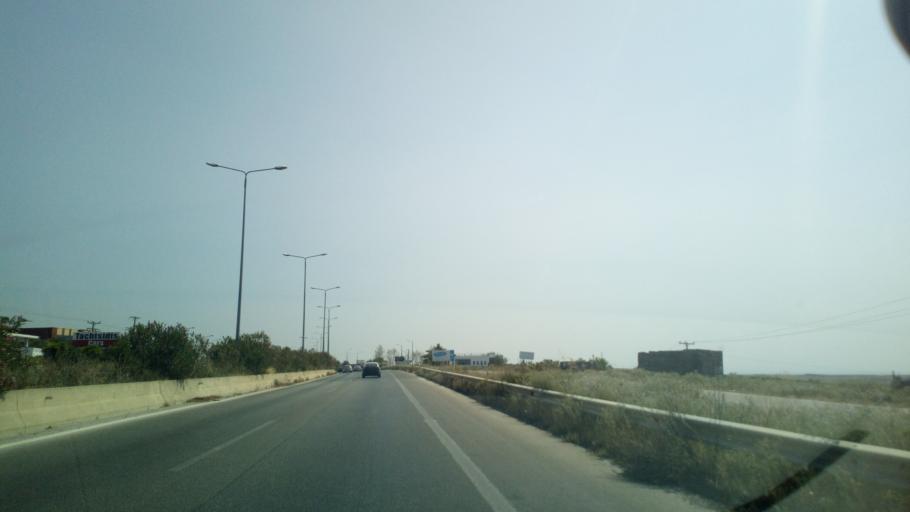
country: GR
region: Central Macedonia
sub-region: Nomos Thessalonikis
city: Mesimeri
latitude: 40.4011
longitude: 23.0309
